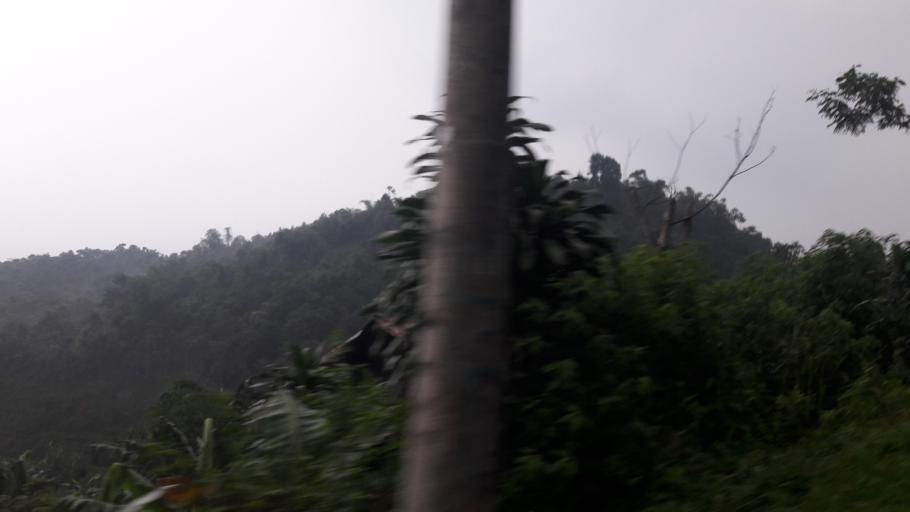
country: ID
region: West Java
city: Cipeundeuy
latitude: -6.6550
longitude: 106.5170
